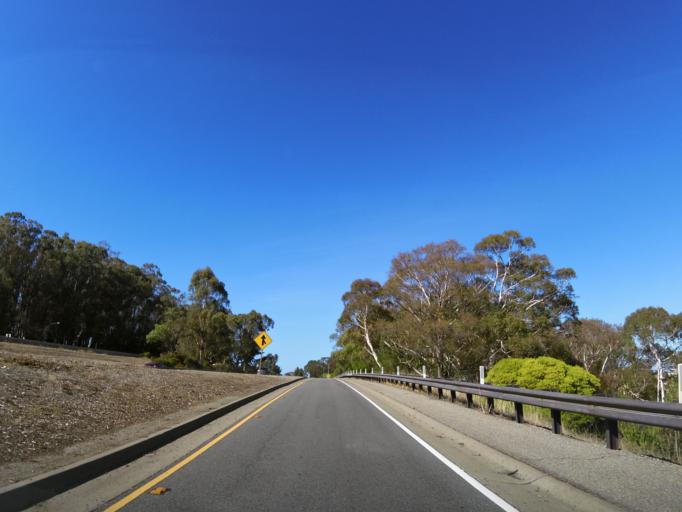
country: US
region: California
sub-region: San Mateo County
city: Millbrae
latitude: 37.5823
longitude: -122.4042
